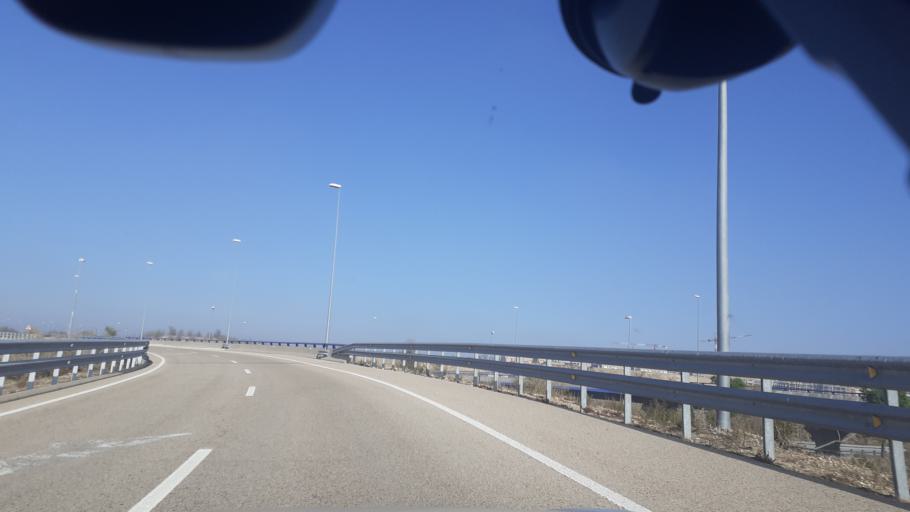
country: ES
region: Madrid
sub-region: Provincia de Madrid
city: Coslada
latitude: 40.4001
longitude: -3.5725
